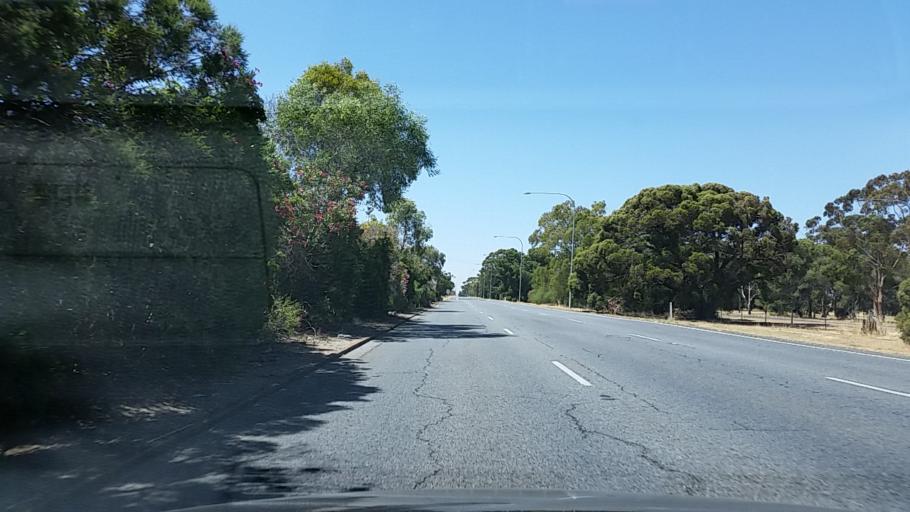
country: AU
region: South Australia
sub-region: Playford
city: Smithfield
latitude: -34.6983
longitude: 138.6839
